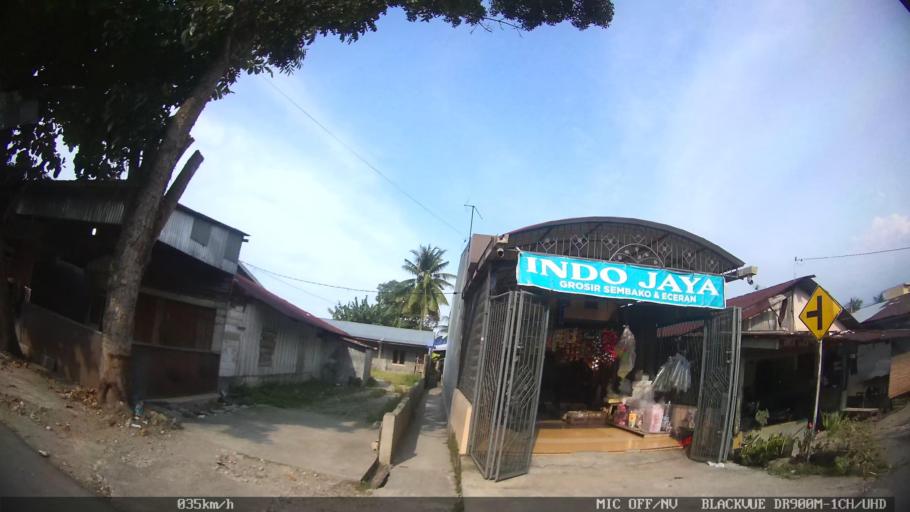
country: ID
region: North Sumatra
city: Binjai
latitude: 3.6033
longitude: 98.4958
